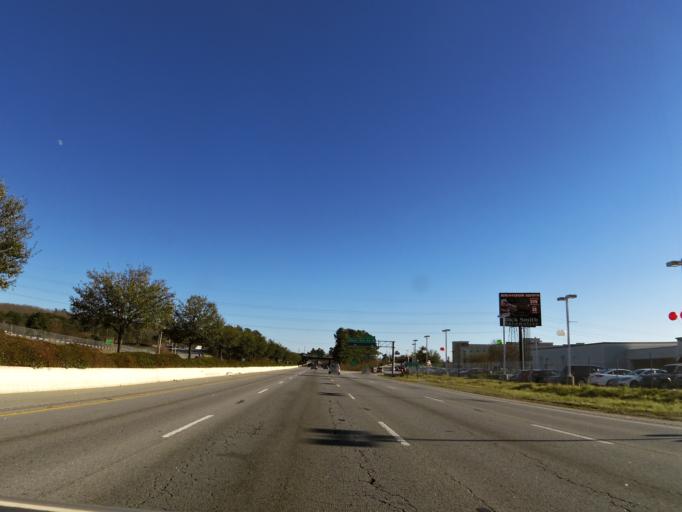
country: US
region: South Carolina
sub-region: Greenville County
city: Wade Hampton
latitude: 34.8422
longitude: -82.3176
